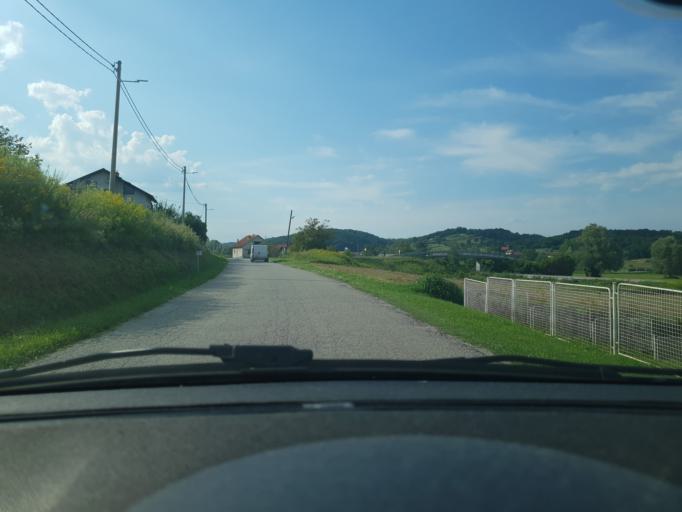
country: HR
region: Zagrebacka
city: Jakovlje
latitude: 46.0340
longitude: 15.8263
